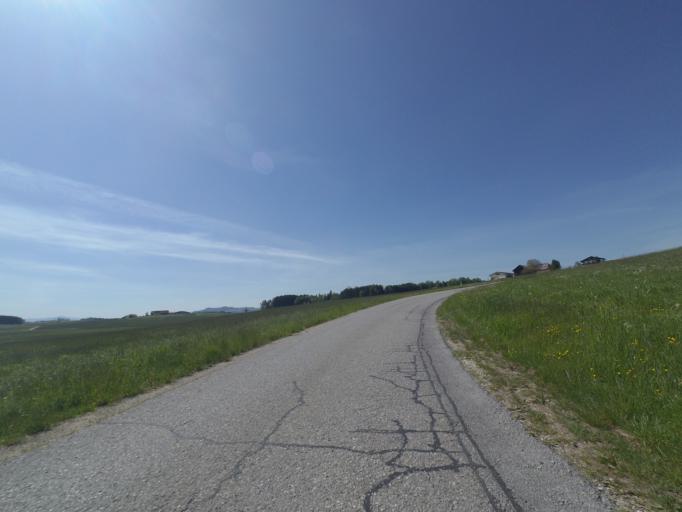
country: AT
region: Salzburg
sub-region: Politischer Bezirk Salzburg-Umgebung
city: Seekirchen am Wallersee
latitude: 47.9243
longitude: 13.1246
